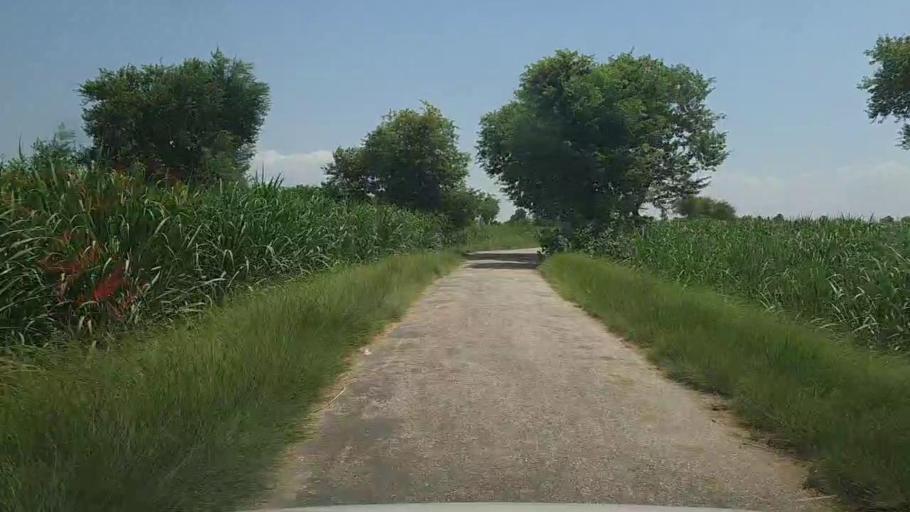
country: PK
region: Sindh
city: Ubauro
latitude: 28.1575
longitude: 69.7476
